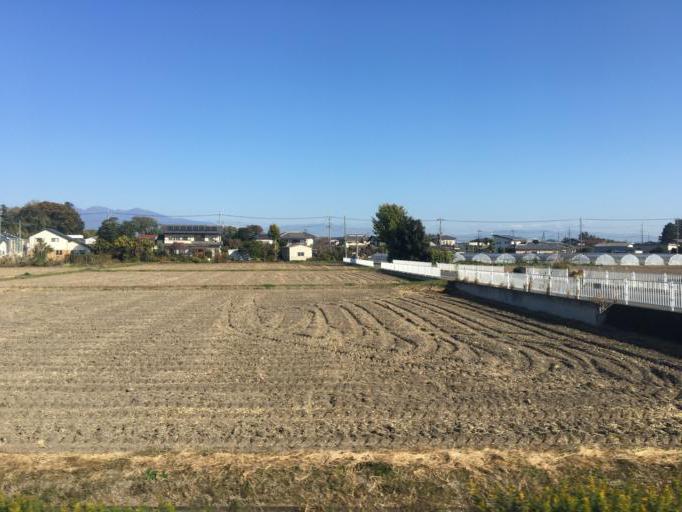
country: JP
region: Gunma
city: Isesaki
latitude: 36.3465
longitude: 139.1578
